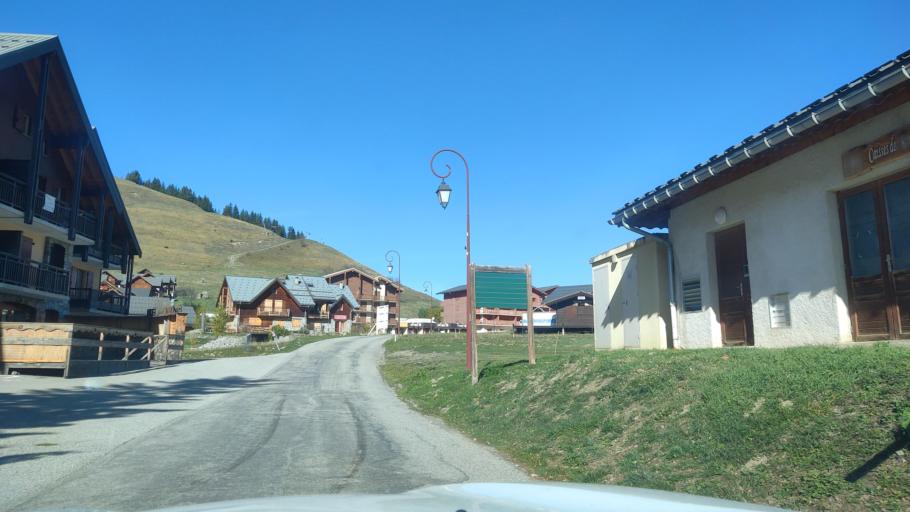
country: FR
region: Rhone-Alpes
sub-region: Departement de la Savoie
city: Villargondran
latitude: 45.2074
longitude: 6.3373
